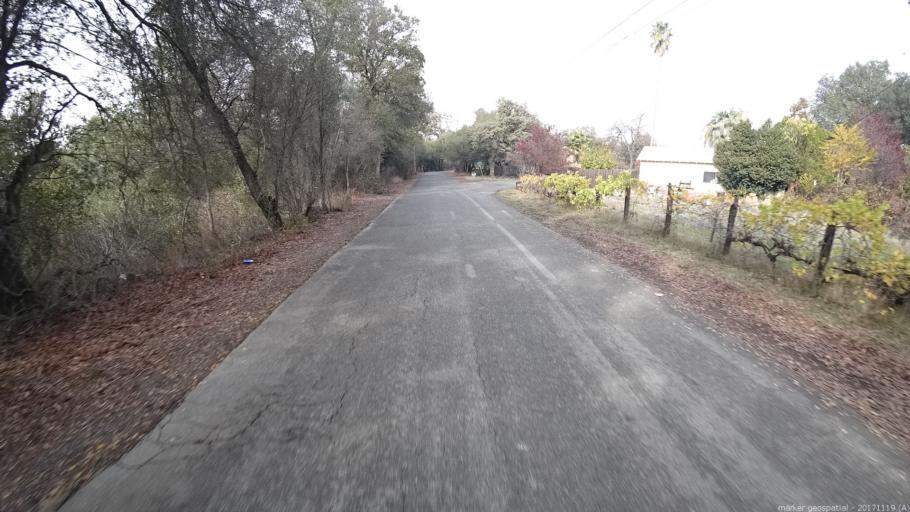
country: US
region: California
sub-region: Shasta County
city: Anderson
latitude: 40.4772
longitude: -122.3027
